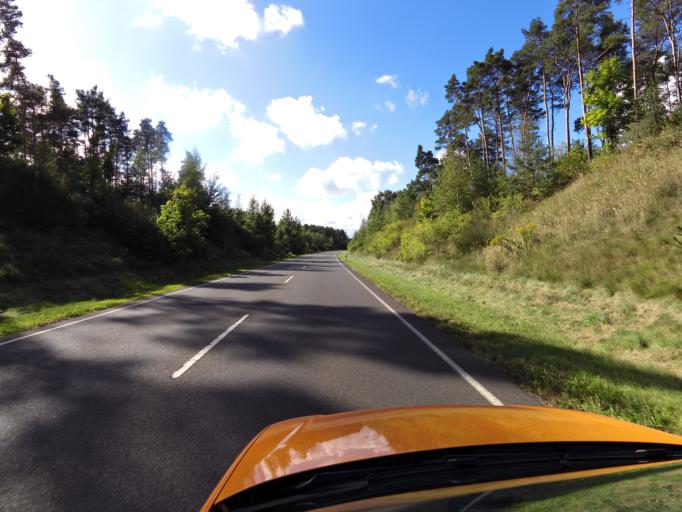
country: DE
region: Brandenburg
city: Michendorf
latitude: 52.3050
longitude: 13.0419
